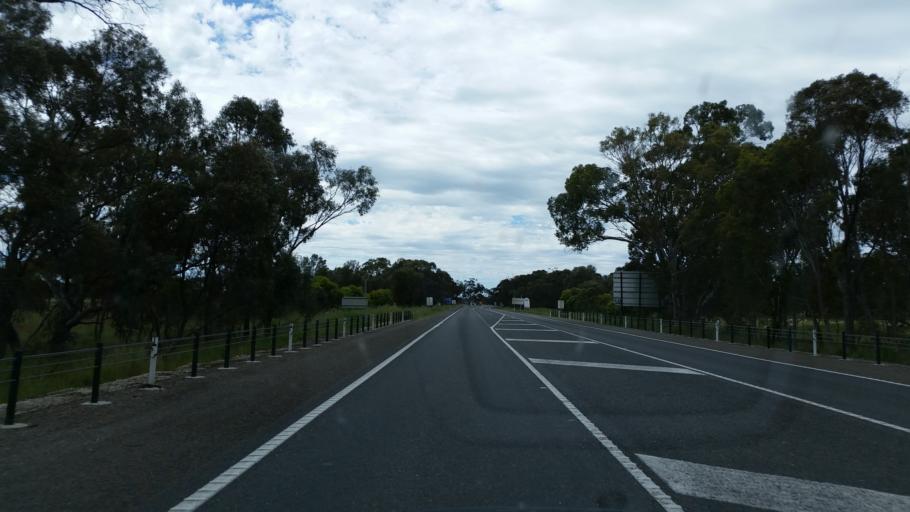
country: AU
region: South Australia
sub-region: Tatiara
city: Bordertown
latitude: -36.3435
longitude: 140.9632
